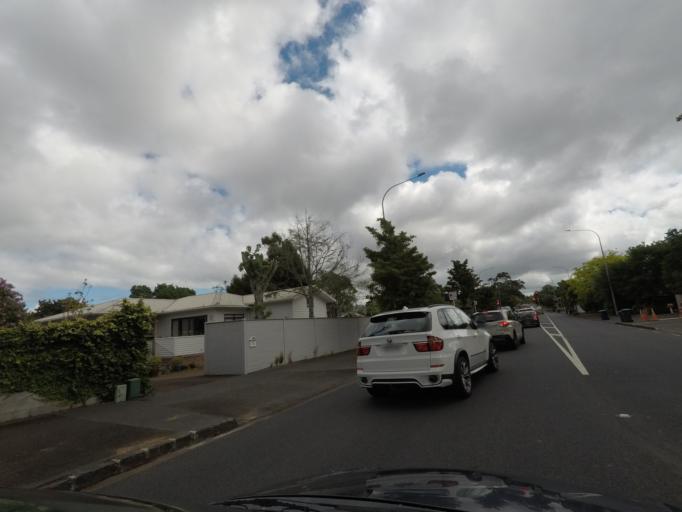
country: NZ
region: Auckland
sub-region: Auckland
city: Auckland
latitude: -36.8848
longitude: 174.8041
